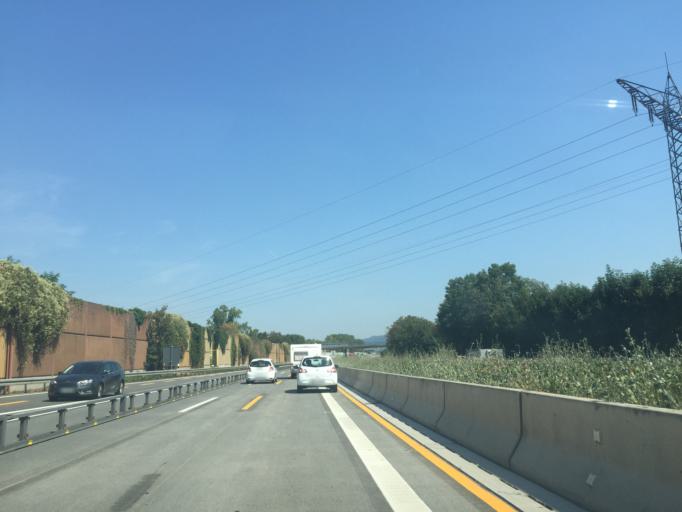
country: DE
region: Baden-Wuerttemberg
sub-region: Karlsruhe Region
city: Eppelheim
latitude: 49.3756
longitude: 8.6329
